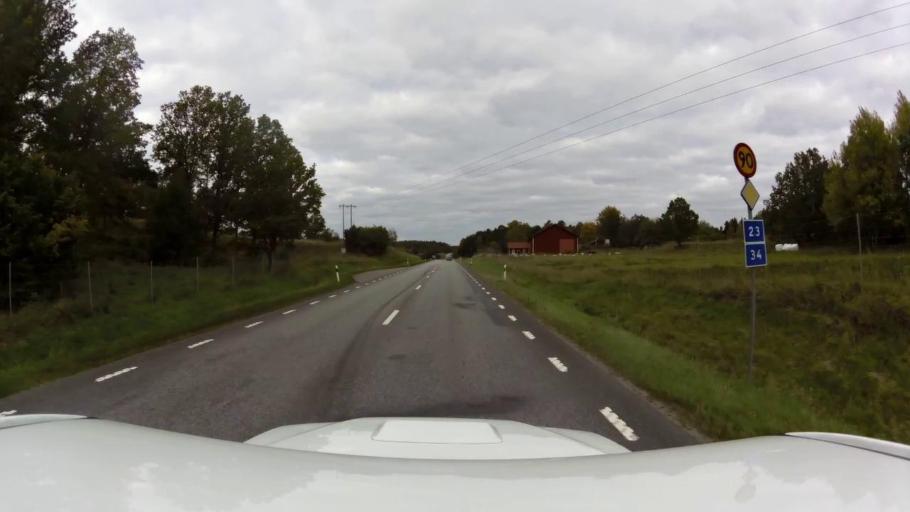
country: SE
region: OEstergoetland
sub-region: Kinda Kommun
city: Rimforsa
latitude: 58.2300
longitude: 15.6446
